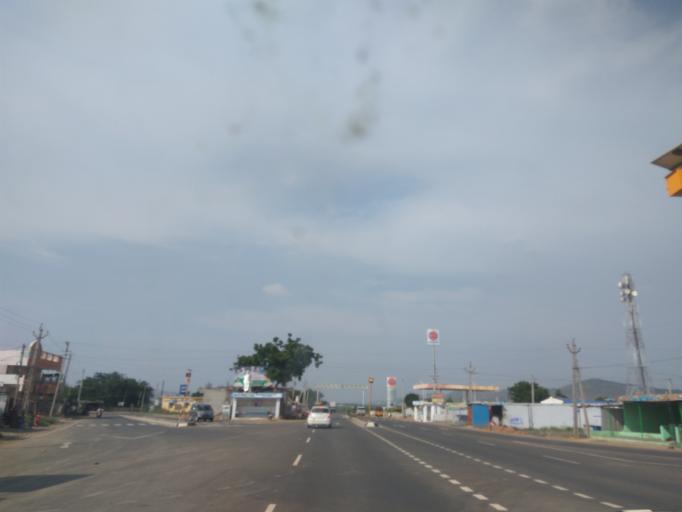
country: IN
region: Andhra Pradesh
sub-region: Prakasam
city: Markapur
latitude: 15.7954
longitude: 79.2569
